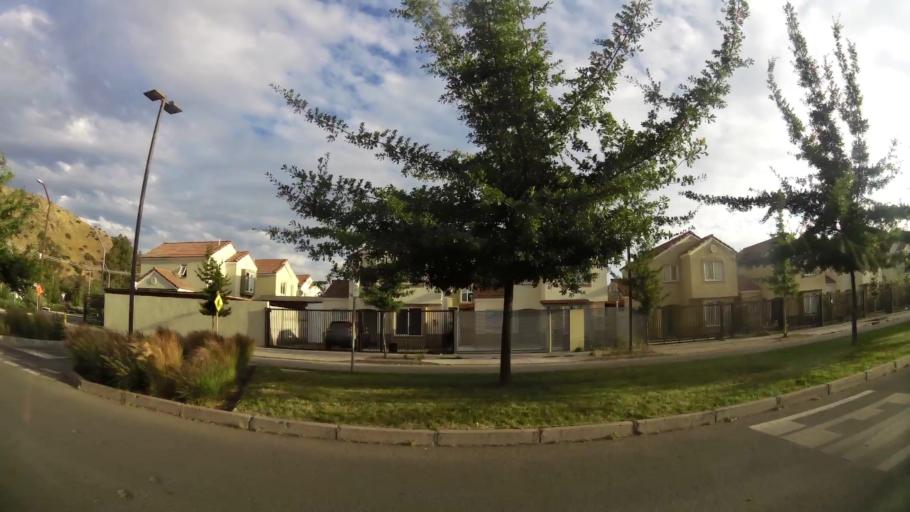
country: CL
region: Santiago Metropolitan
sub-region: Provincia de Maipo
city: San Bernardo
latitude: -33.6274
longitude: -70.6801
